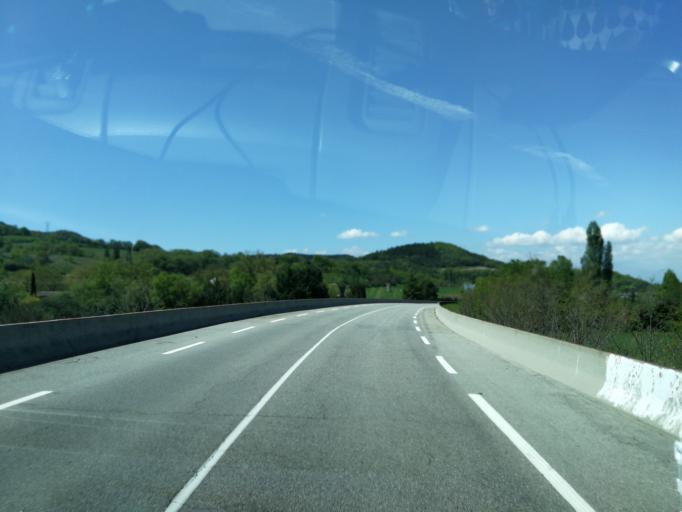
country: FR
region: Rhone-Alpes
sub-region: Departement de la Drome
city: Aouste-sur-Sye
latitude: 44.7032
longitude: 5.0935
